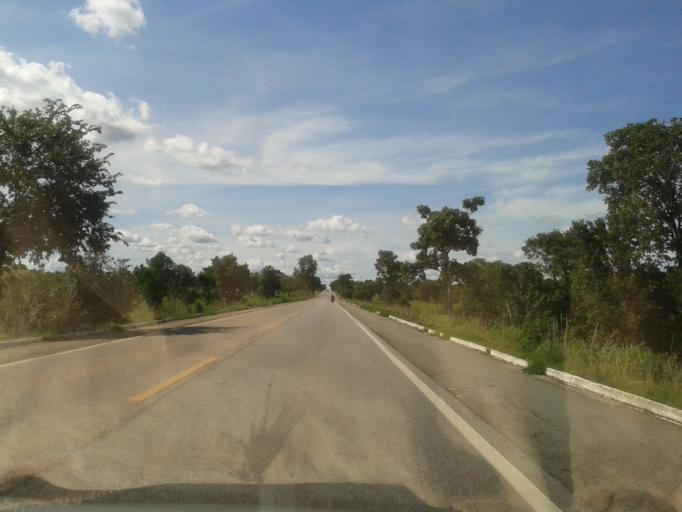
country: BR
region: Goias
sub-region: Mozarlandia
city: Mozarlandia
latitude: -15.2691
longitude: -50.4852
